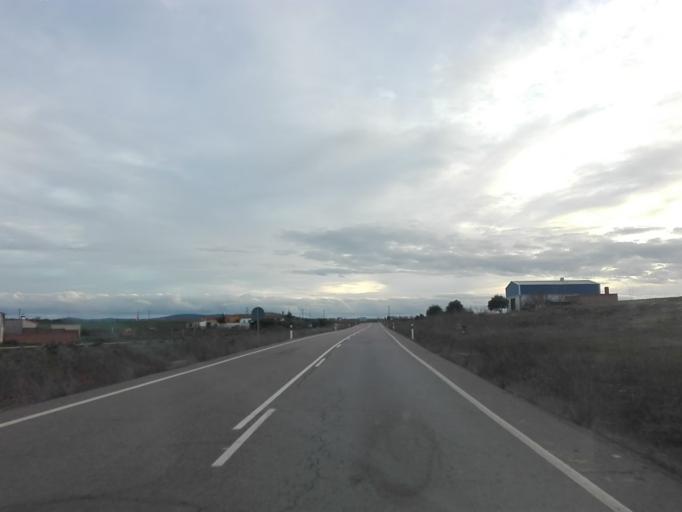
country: ES
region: Extremadura
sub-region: Provincia de Badajoz
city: Usagre
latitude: 38.3495
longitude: -6.1715
